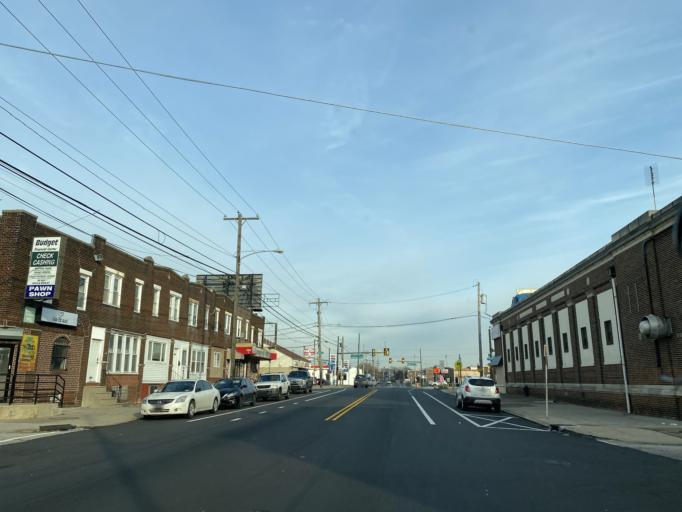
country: US
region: New Jersey
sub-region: Burlington County
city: Palmyra
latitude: 40.0133
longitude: -75.0699
